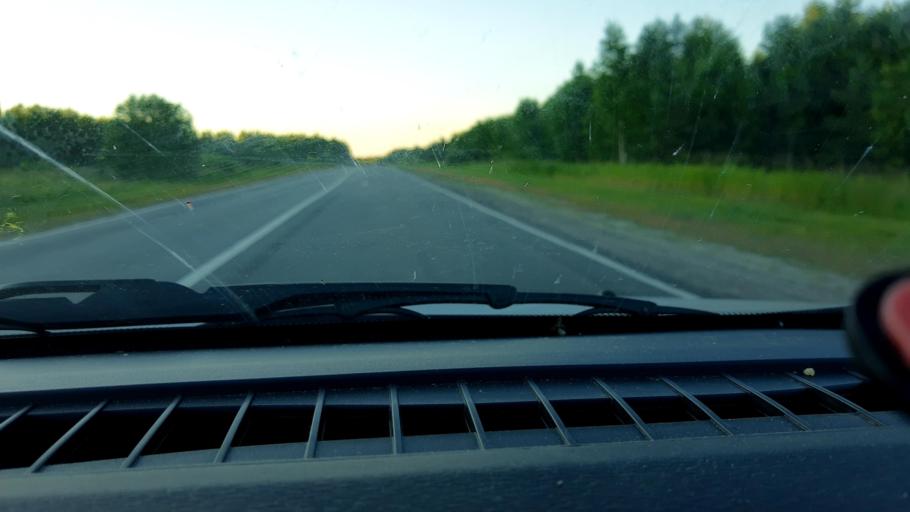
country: RU
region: Nizjnij Novgorod
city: Krasnyye Baki
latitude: 56.9790
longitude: 45.1152
